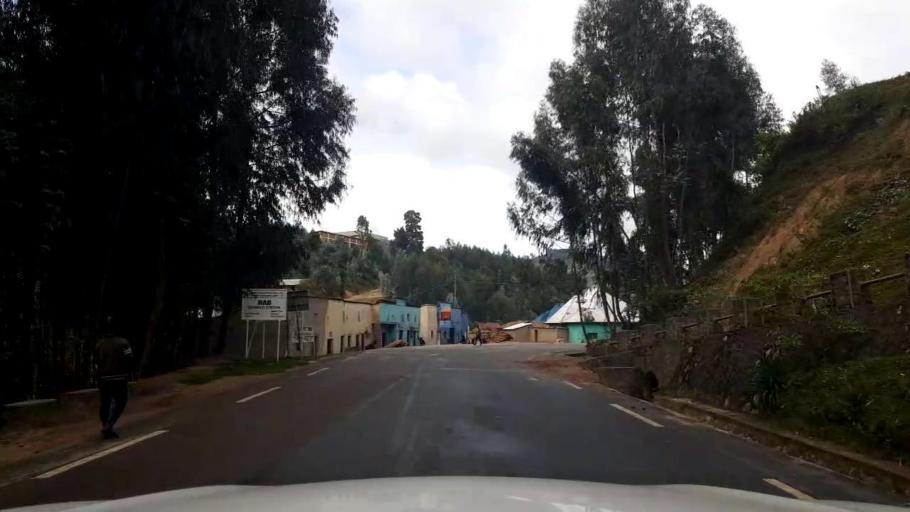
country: RW
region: Northern Province
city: Musanze
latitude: -1.6870
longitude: 29.5197
